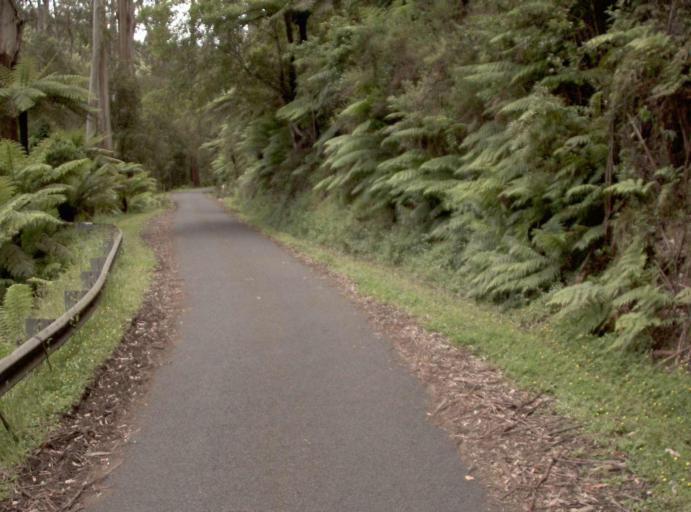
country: AU
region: Victoria
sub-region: Latrobe
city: Traralgon
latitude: -38.4631
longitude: 146.5490
